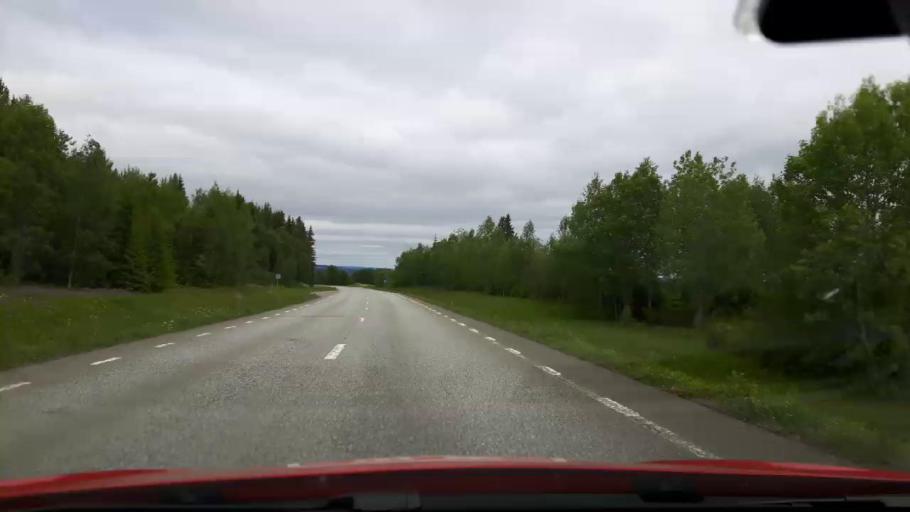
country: SE
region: Jaemtland
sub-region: Krokoms Kommun
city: Krokom
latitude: 63.5749
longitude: 14.6307
